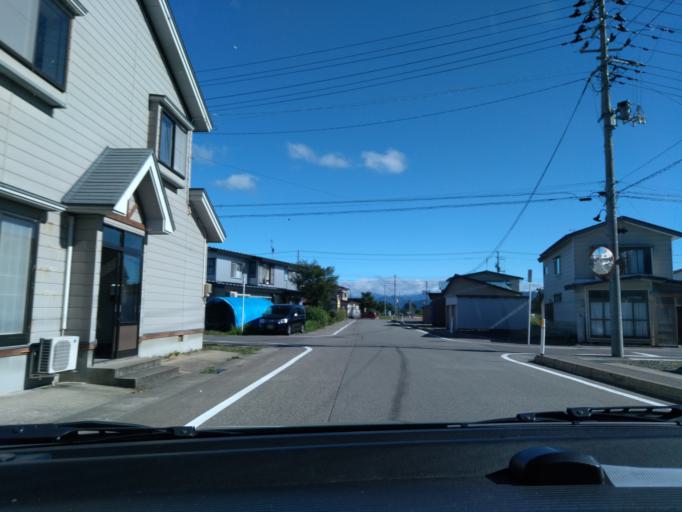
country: JP
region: Akita
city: Yuzawa
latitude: 39.2026
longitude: 140.5514
